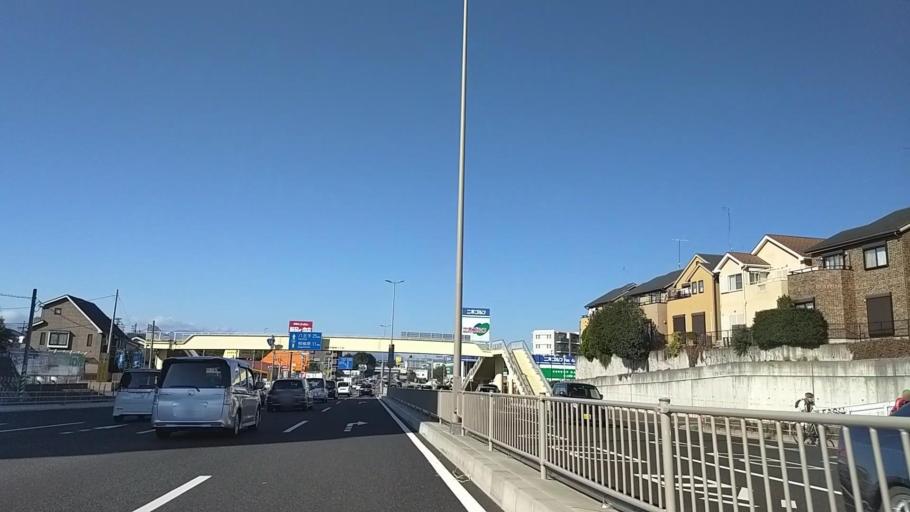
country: JP
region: Tokyo
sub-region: Machida-shi
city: Machida
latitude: 35.5135
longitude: 139.4667
